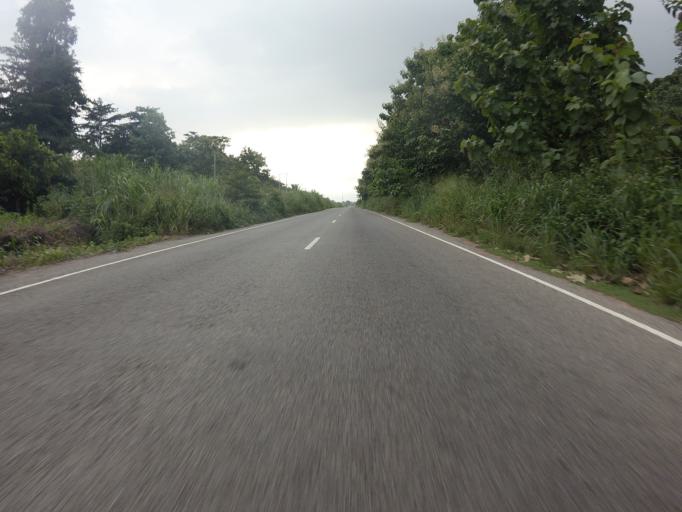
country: GH
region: Volta
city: Ho
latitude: 6.7782
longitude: 0.4707
